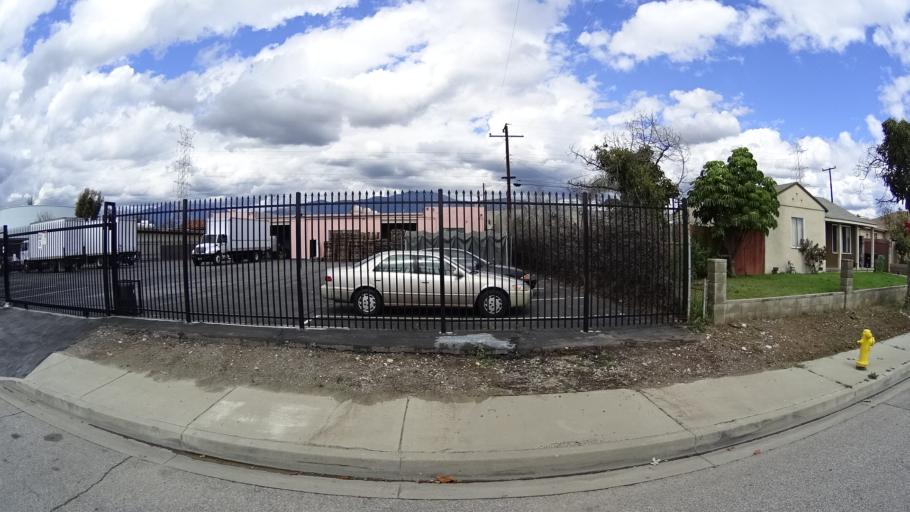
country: US
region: California
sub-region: Los Angeles County
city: Baldwin Park
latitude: 34.1059
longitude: -117.9629
